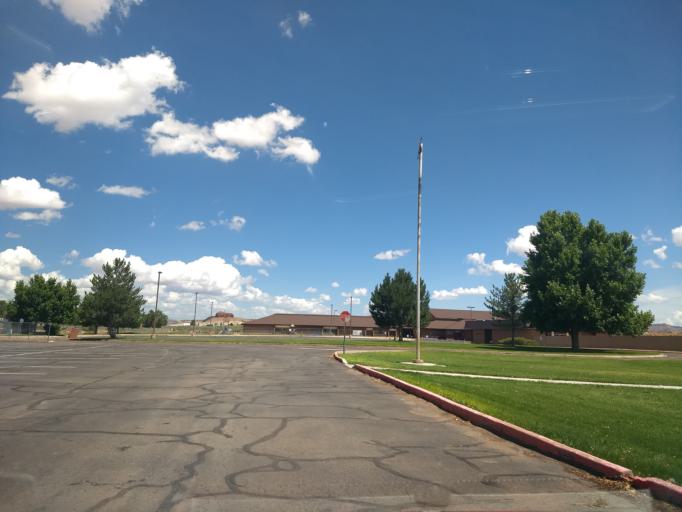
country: US
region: Arizona
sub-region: Coconino County
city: Fredonia
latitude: 36.9518
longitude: -112.5220
